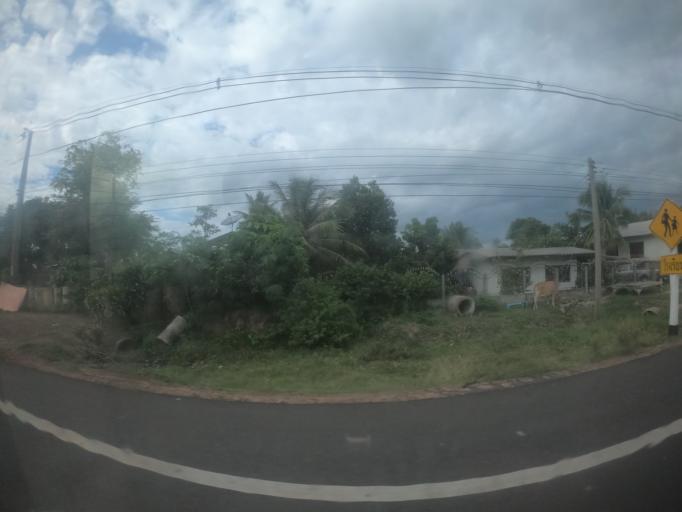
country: TH
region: Surin
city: Prasat
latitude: 14.5656
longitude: 103.4934
